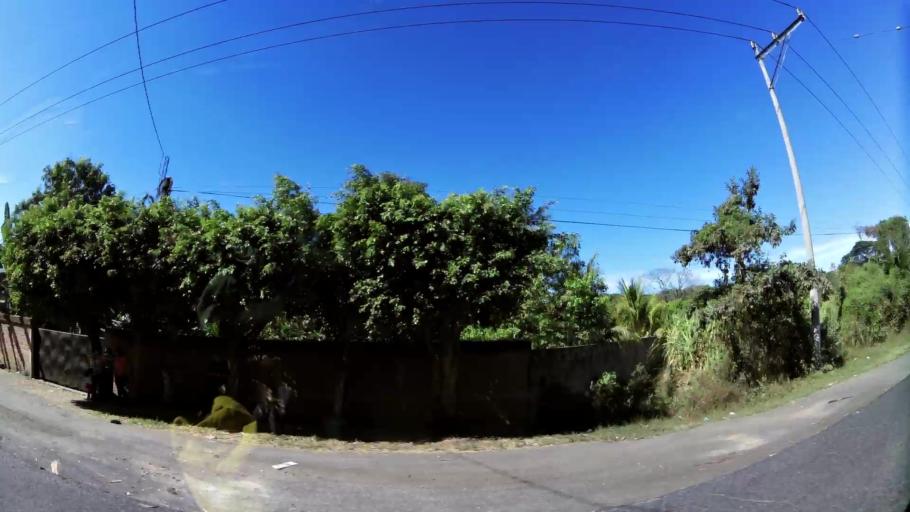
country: SV
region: La Libertad
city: San Juan Opico
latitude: 13.8262
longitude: -89.3535
